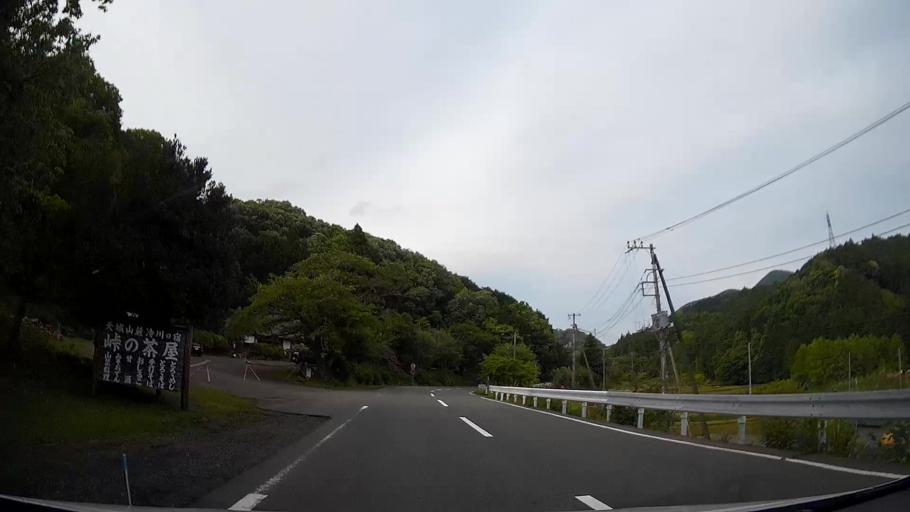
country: JP
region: Shizuoka
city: Ito
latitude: 34.9620
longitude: 139.0353
